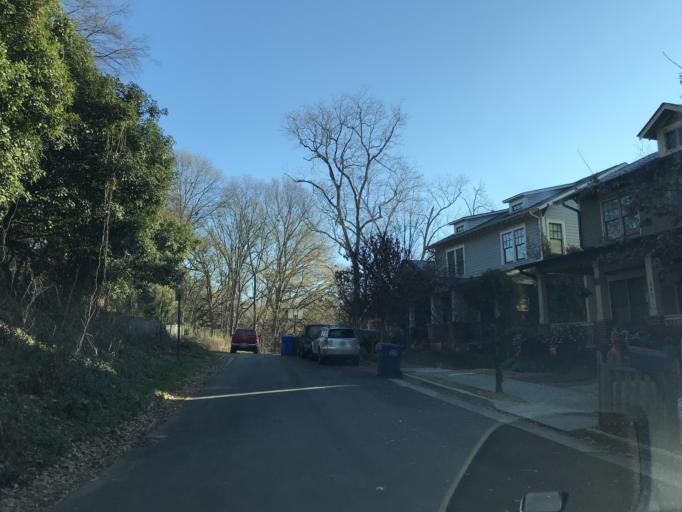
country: US
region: Georgia
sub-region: DeKalb County
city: Druid Hills
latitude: 33.7629
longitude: -84.3567
